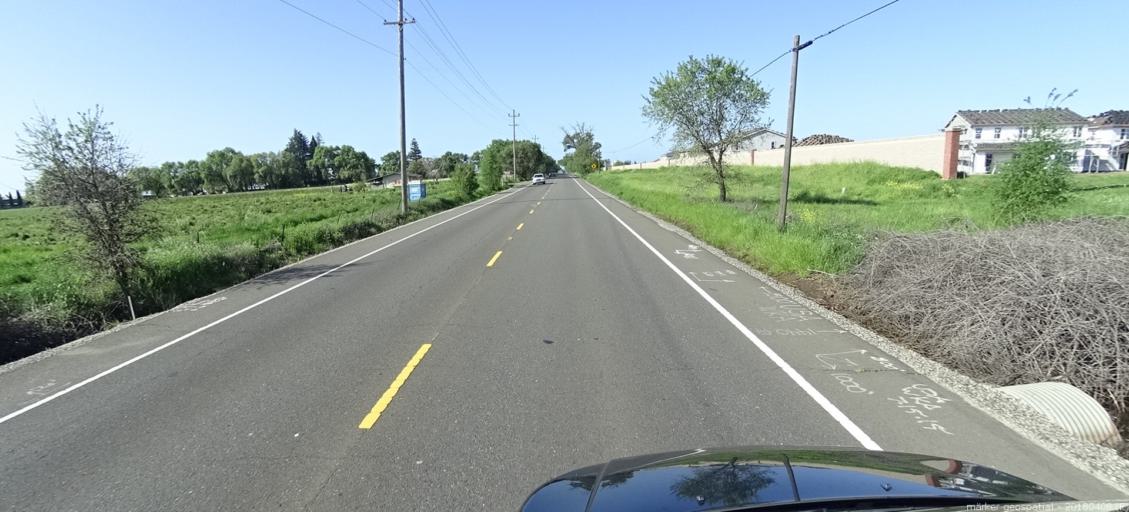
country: US
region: California
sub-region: Sacramento County
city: Elk Grove
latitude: 38.3952
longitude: -121.3393
